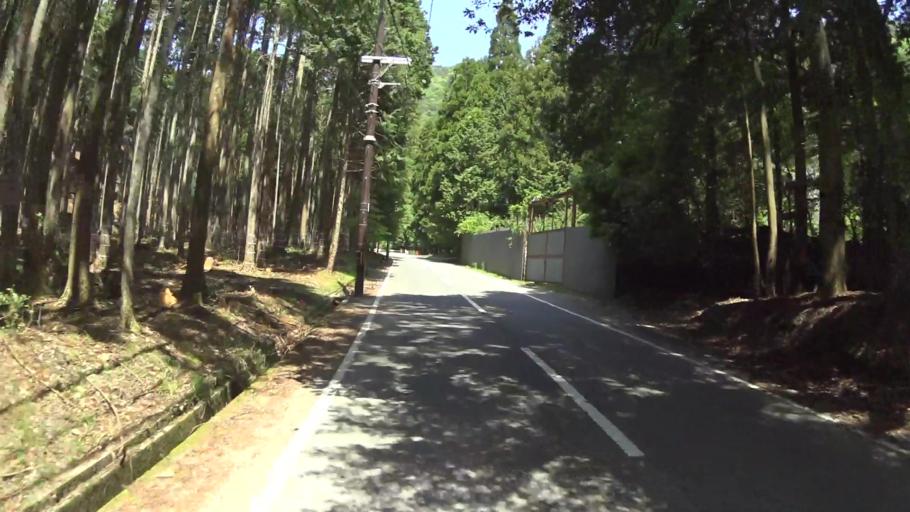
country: JP
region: Shiga Prefecture
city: Kitahama
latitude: 35.1506
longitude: 135.8392
